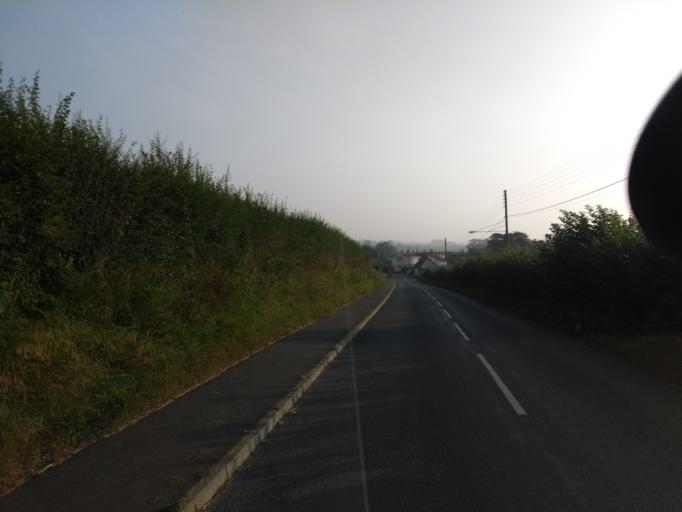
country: GB
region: England
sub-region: Somerset
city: Curry Rivel
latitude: 50.9925
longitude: -2.8614
